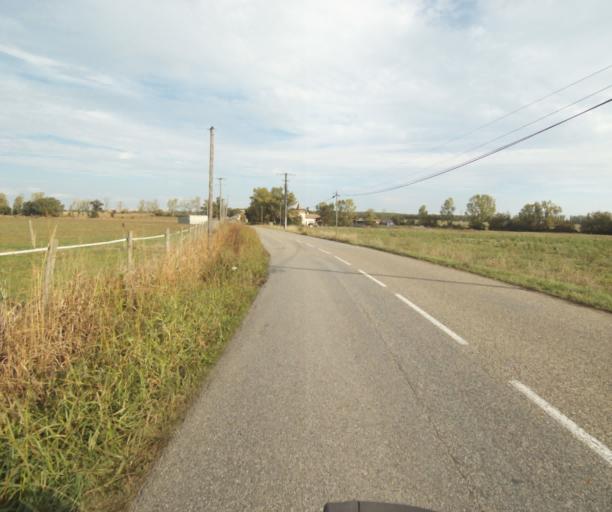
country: FR
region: Midi-Pyrenees
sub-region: Departement du Tarn-et-Garonne
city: Montech
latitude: 43.9722
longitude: 1.2326
